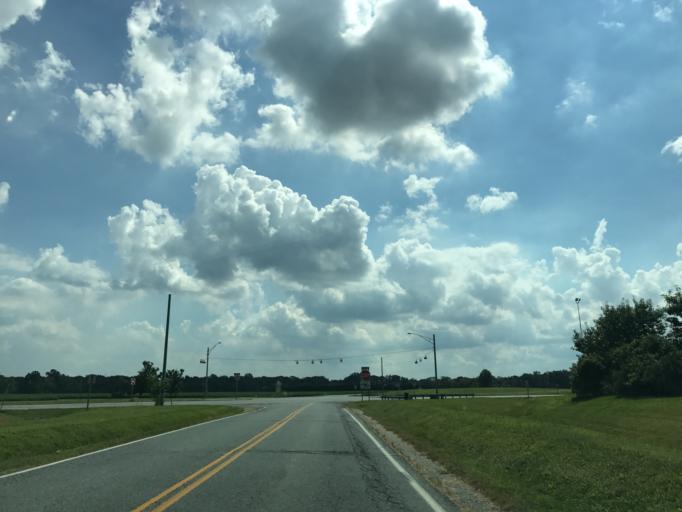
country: US
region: Delaware
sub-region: New Castle County
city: Middletown
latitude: 39.3857
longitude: -75.7999
